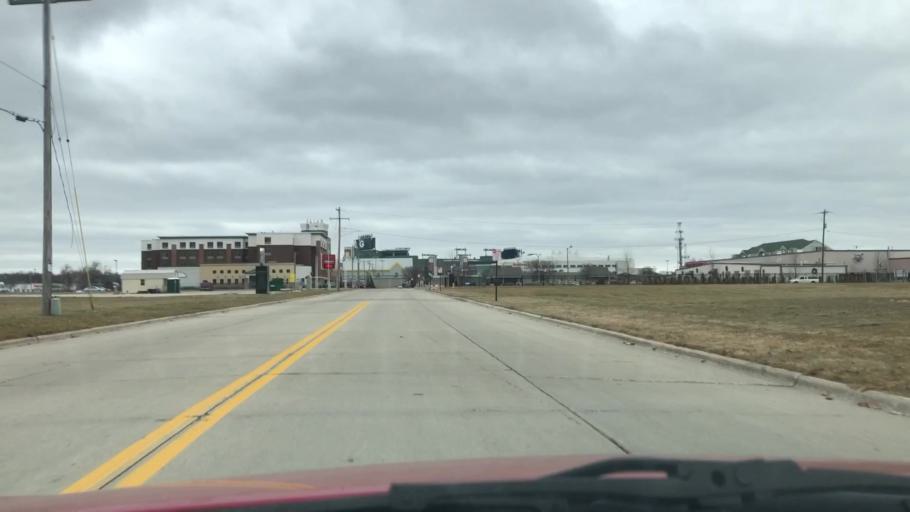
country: US
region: Wisconsin
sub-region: Brown County
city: Ashwaubenon
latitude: 44.4958
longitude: -88.0480
